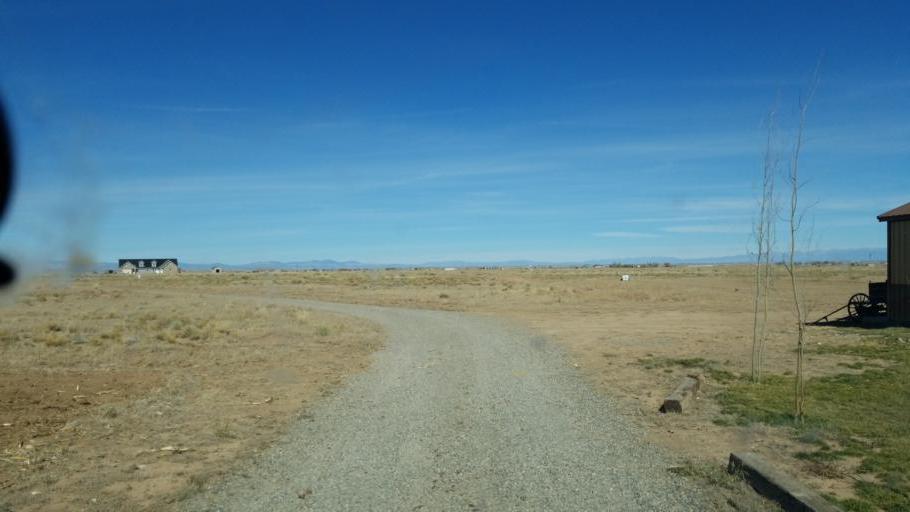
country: US
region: Colorado
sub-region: Rio Grande County
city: Monte Vista
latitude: 37.3995
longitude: -106.1190
